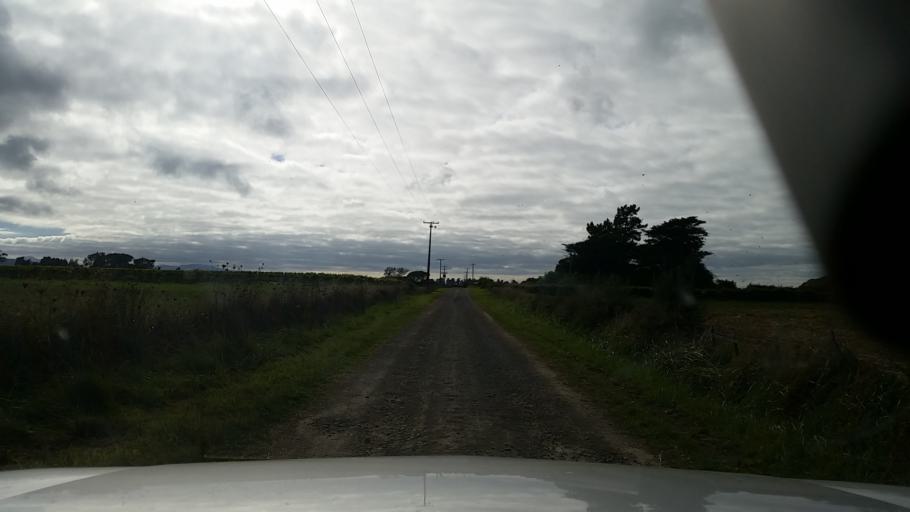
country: NZ
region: Marlborough
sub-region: Marlborough District
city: Blenheim
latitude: -41.4635
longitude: 173.9924
